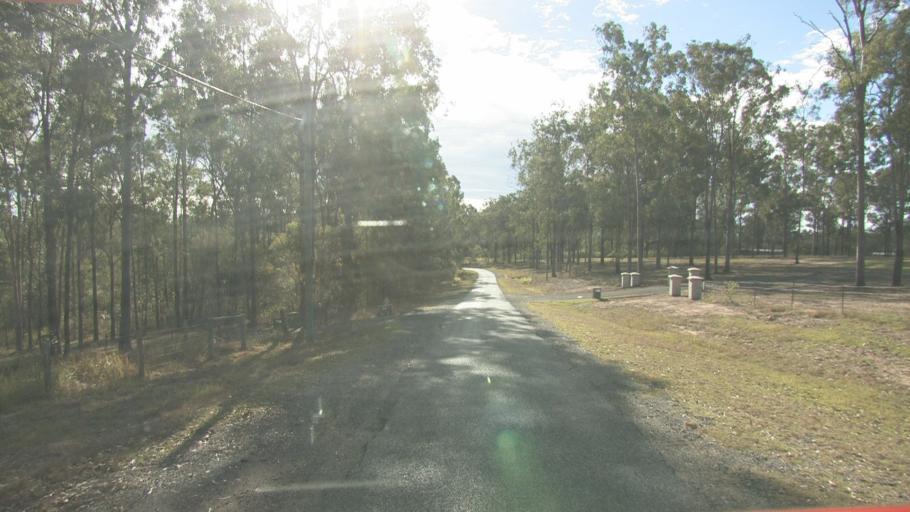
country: AU
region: Queensland
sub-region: Logan
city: Cedar Vale
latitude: -27.8409
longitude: 153.0679
